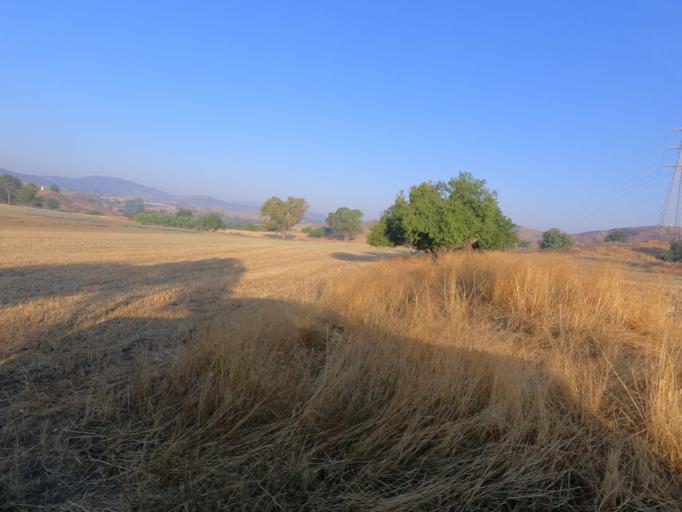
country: CY
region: Larnaka
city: Mosfiloti
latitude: 34.9753
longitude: 33.4313
